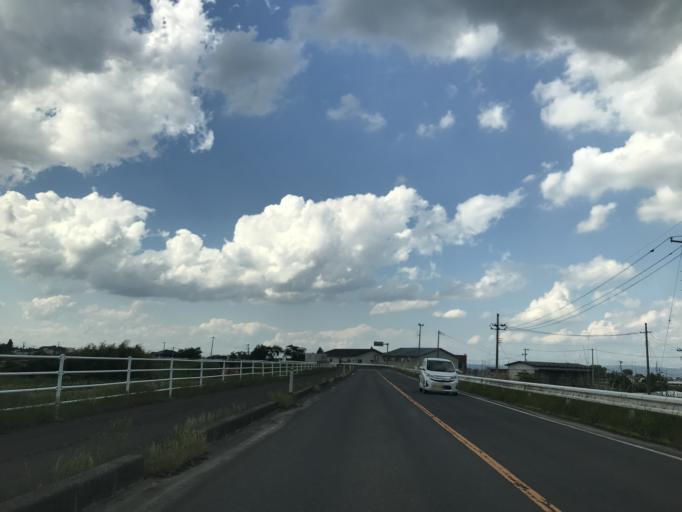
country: JP
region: Miyagi
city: Wakuya
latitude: 38.6491
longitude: 141.2174
